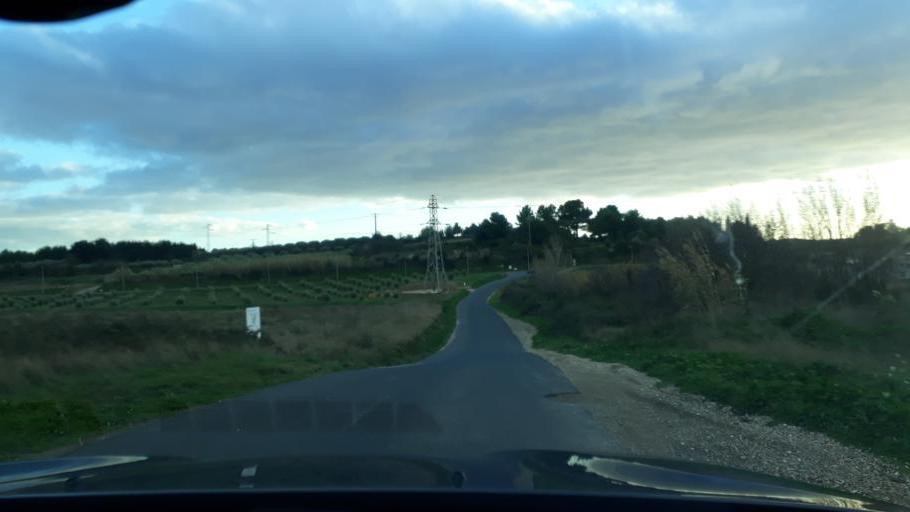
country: FR
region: Languedoc-Roussillon
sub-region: Departement de l'Herault
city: Nissan-lez-Enserune
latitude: 43.2943
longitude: 3.1313
